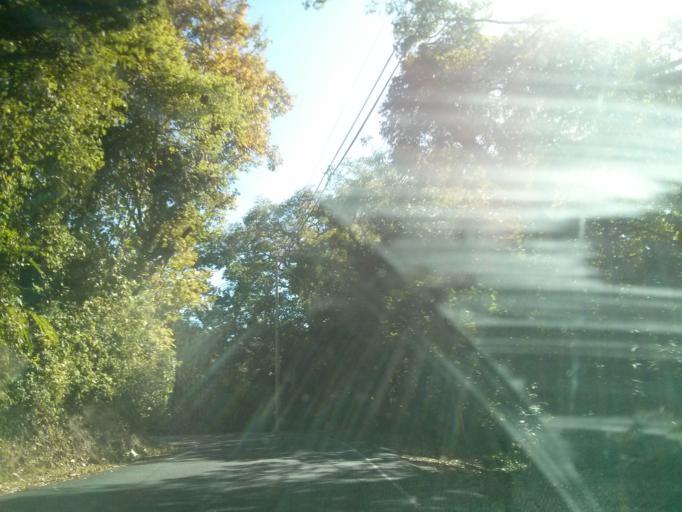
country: CR
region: Puntarenas
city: Paquera
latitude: 9.7784
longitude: -84.9527
